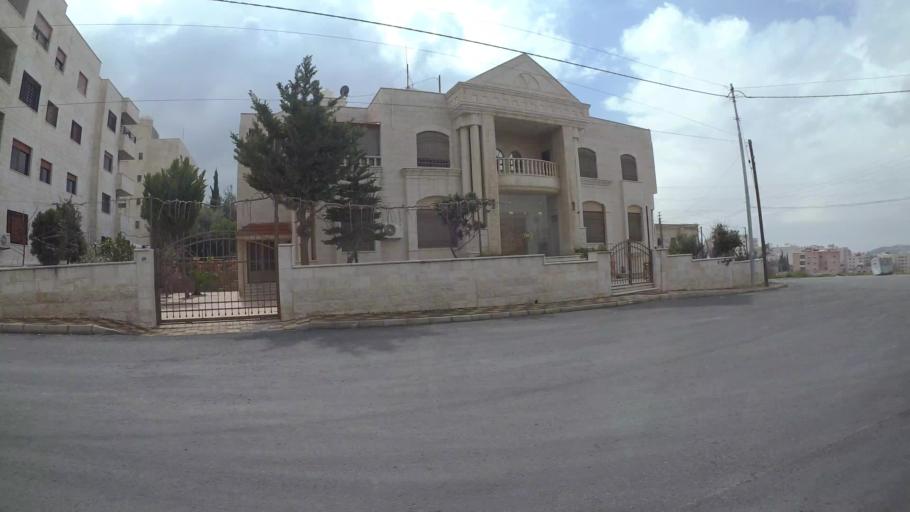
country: JO
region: Amman
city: Umm as Summaq
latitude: 31.8989
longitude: 35.8350
